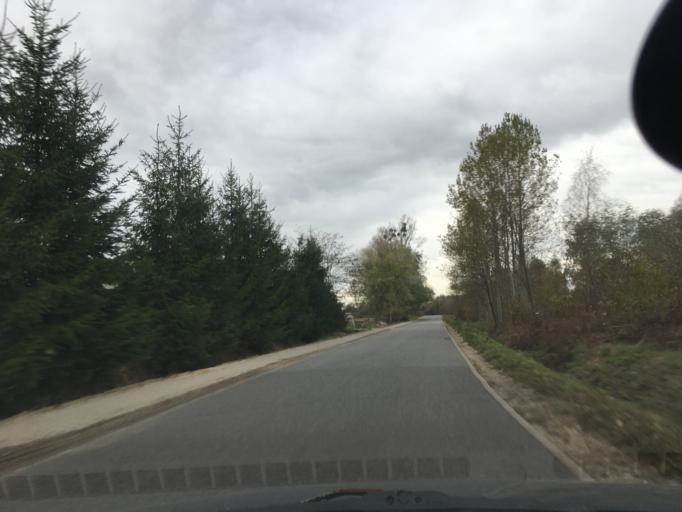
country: PL
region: Lodz Voivodeship
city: Zabia Wola
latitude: 52.0253
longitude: 20.7068
